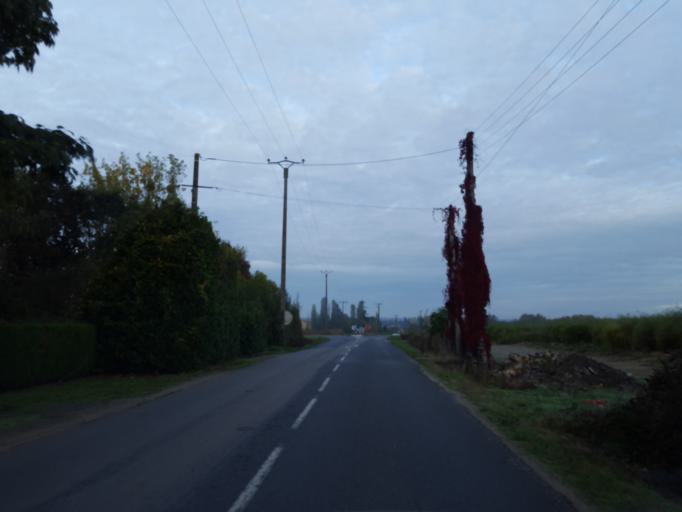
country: FR
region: Pays de la Loire
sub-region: Departement de la Loire-Atlantique
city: Saint-Julien-de-Concelles
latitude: 47.2466
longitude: -1.3997
